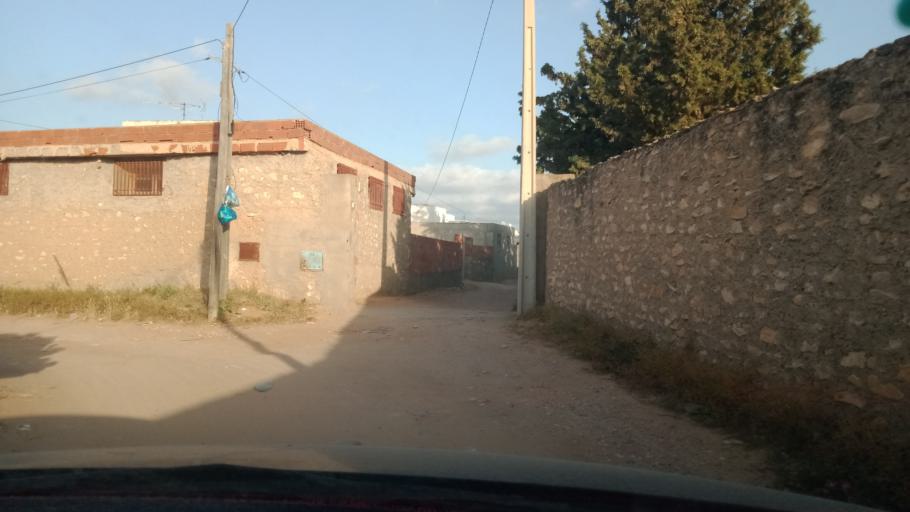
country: TN
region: Safaqis
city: Al Qarmadah
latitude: 34.8180
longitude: 10.7491
